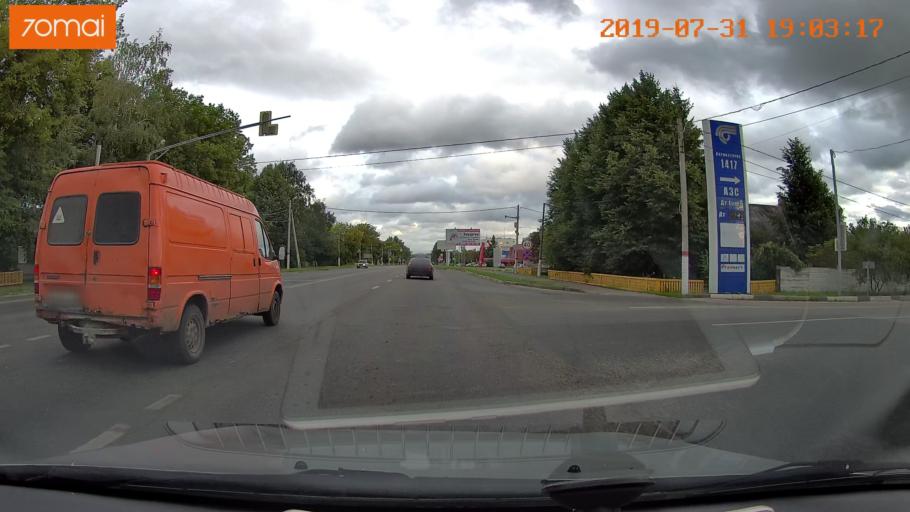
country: RU
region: Moskovskaya
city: Raduzhnyy
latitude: 55.1156
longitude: 38.7368
